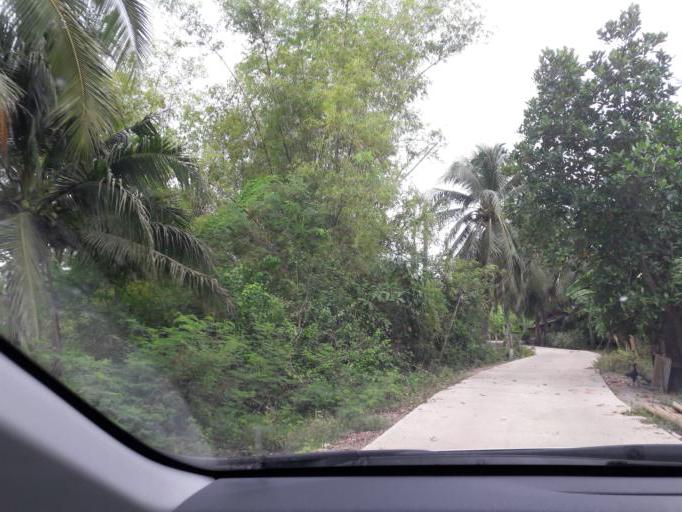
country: TH
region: Samut Sakhon
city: Ban Phaeo
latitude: 13.5963
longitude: 100.0274
